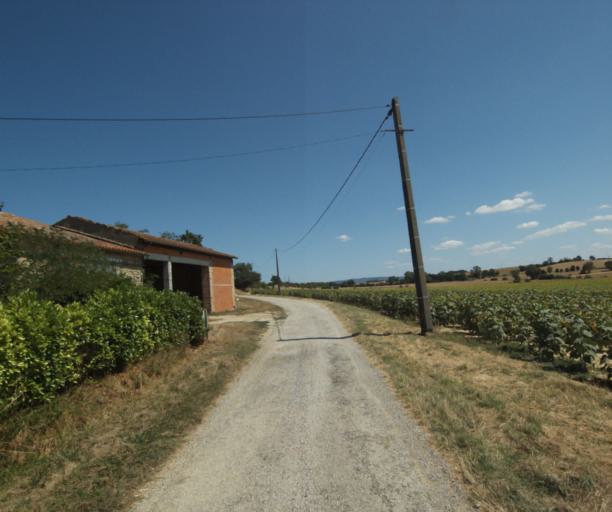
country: FR
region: Midi-Pyrenees
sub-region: Departement de la Haute-Garonne
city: Saint-Felix-Lauragais
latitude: 43.4875
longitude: 1.8917
